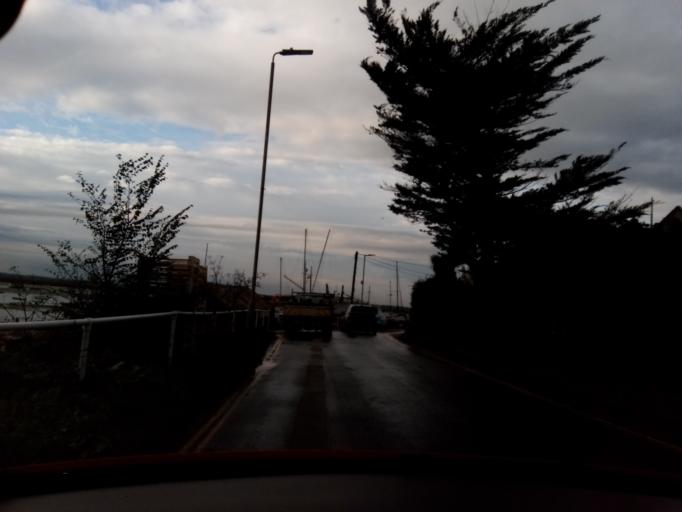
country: GB
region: England
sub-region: Essex
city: West Mersea
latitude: 51.7778
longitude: 0.8993
